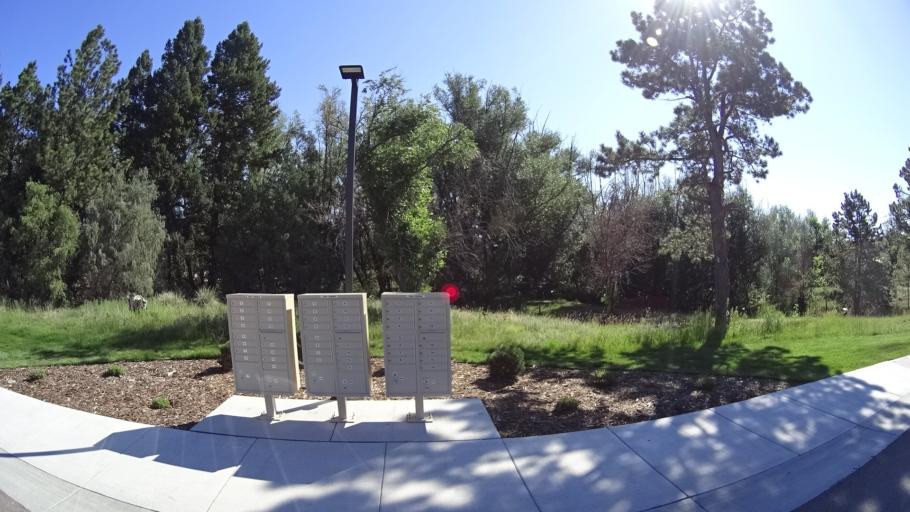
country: US
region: Colorado
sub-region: El Paso County
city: Black Forest
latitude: 38.9828
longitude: -104.7745
